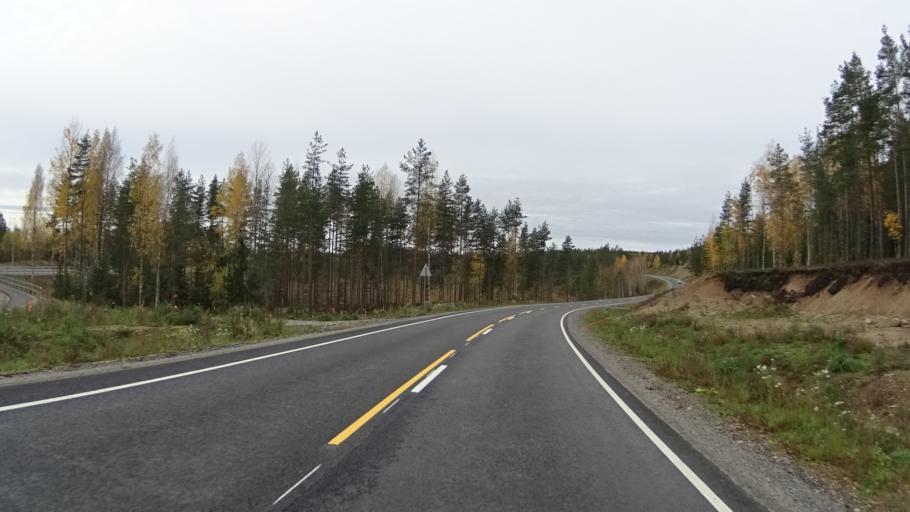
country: FI
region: South Karelia
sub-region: Lappeenranta
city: Luumaeki
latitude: 60.9369
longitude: 27.6736
